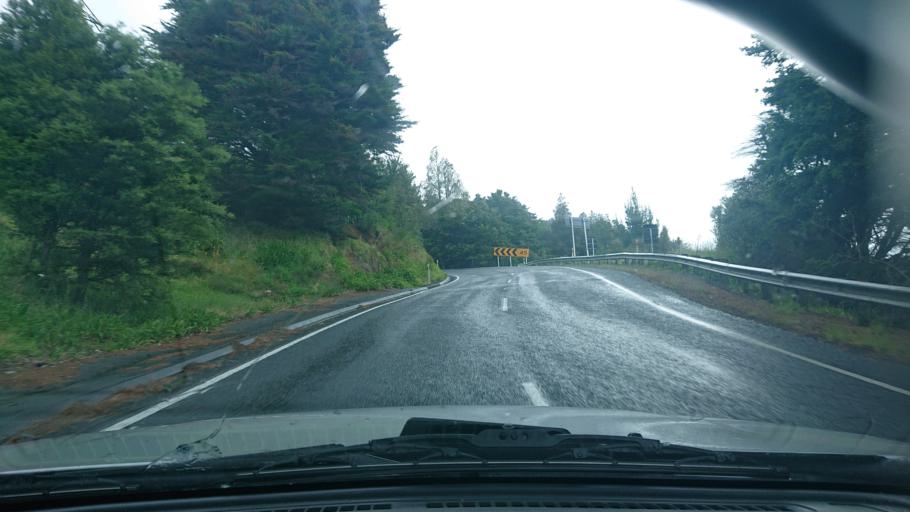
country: NZ
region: Auckland
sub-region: Auckland
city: Wellsford
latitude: -36.3437
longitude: 174.4764
